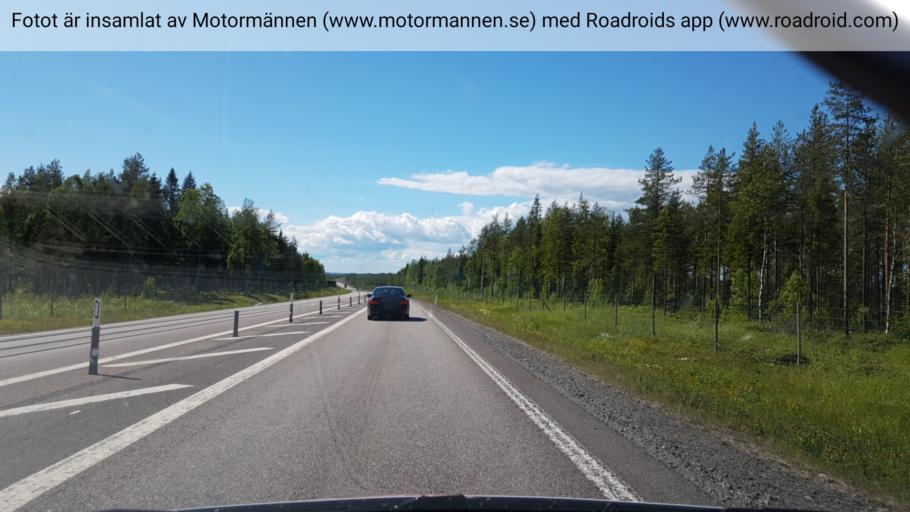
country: SE
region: Norrbotten
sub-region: Kalix Kommun
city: Toere
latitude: 65.9178
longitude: 22.7566
